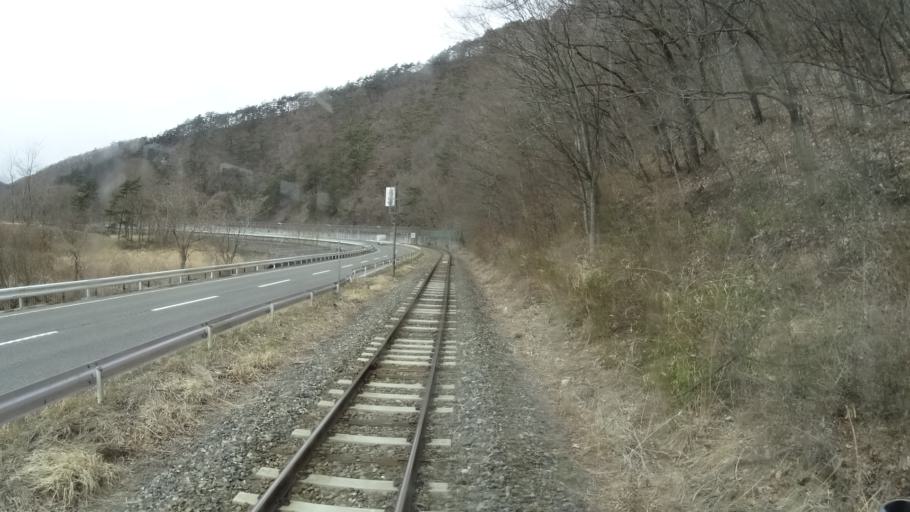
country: JP
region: Iwate
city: Tono
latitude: 39.3032
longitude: 141.3928
